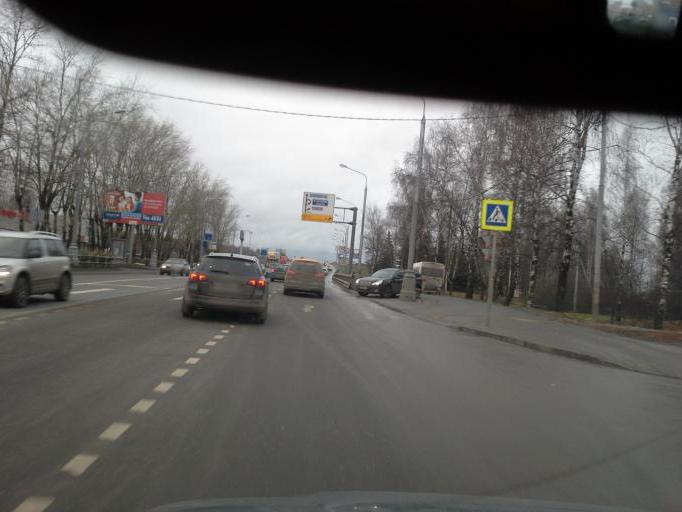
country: RU
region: Moskovskaya
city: Moskovskiy
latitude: 55.6048
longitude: 37.3555
